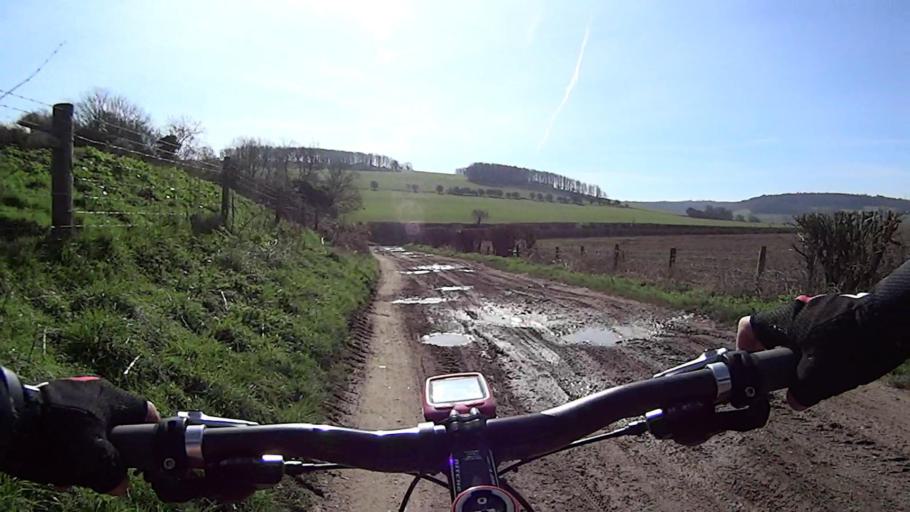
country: GB
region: England
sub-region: West Sussex
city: Boxgrove
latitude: 50.9187
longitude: -0.7340
